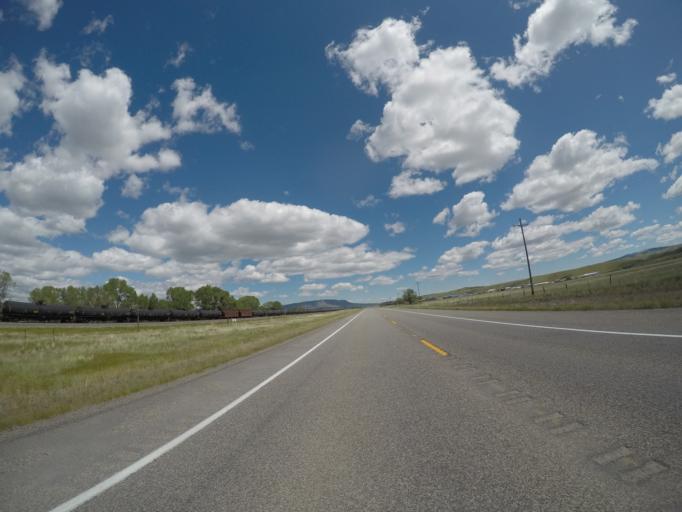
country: US
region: Montana
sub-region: Park County
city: Livingston
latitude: 45.6798
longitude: -110.5243
